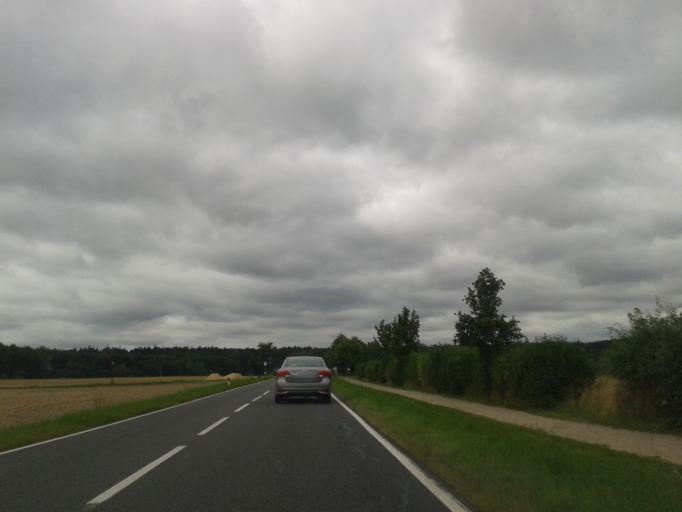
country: DE
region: Saxony
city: Tharandt
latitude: 50.9777
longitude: 13.5602
